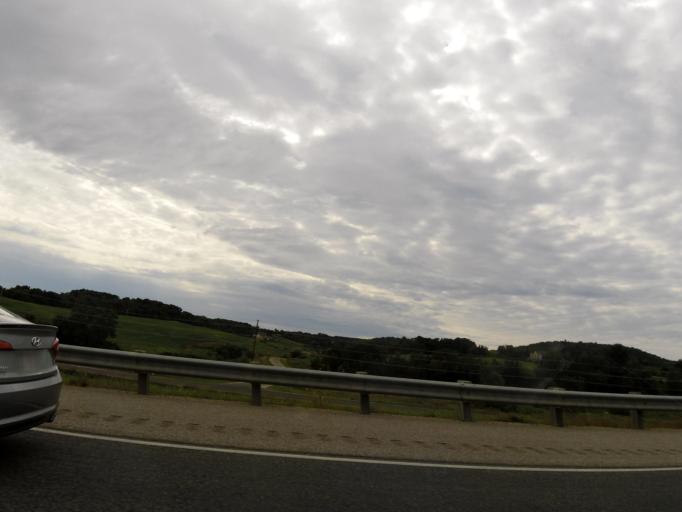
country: US
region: Wisconsin
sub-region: Monroe County
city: Tomah
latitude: 43.9396
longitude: -90.5909
